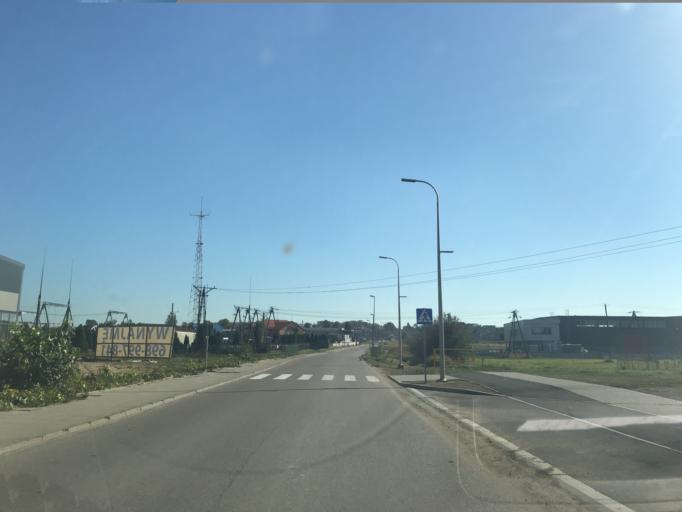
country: PL
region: Warmian-Masurian Voivodeship
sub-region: Powiat ilawski
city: Lubawa
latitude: 53.5121
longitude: 19.7370
